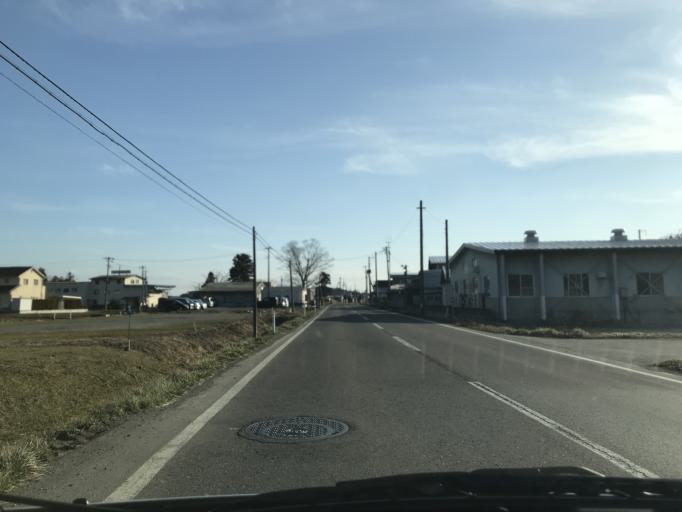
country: JP
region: Iwate
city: Kitakami
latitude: 39.2697
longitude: 141.1175
